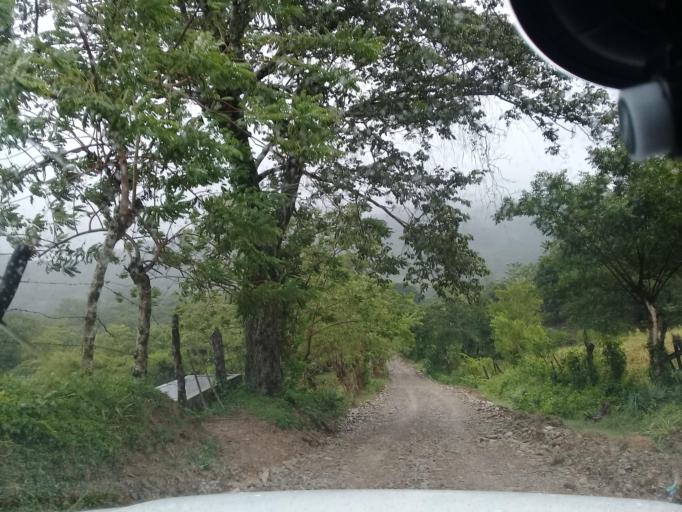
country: MX
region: Veracruz
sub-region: Chalma
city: San Pedro Coyutla
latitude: 21.2301
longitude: -98.4475
